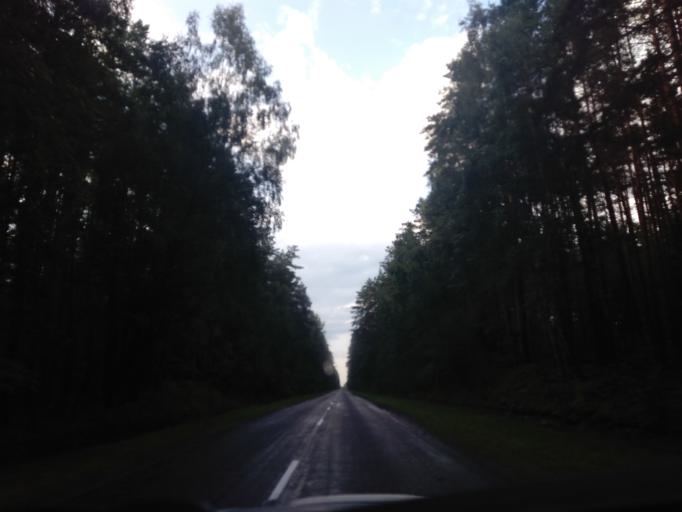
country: BY
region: Minsk
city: Uzda
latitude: 53.3648
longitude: 27.1018
